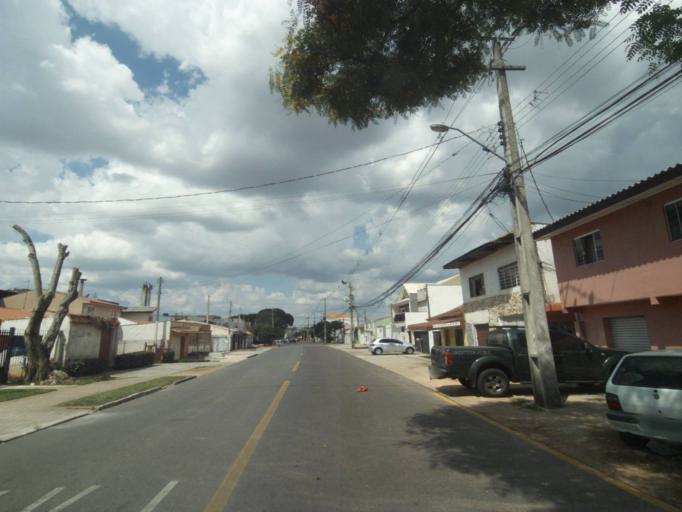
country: BR
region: Parana
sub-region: Sao Jose Dos Pinhais
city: Sao Jose dos Pinhais
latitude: -25.5343
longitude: -49.2637
